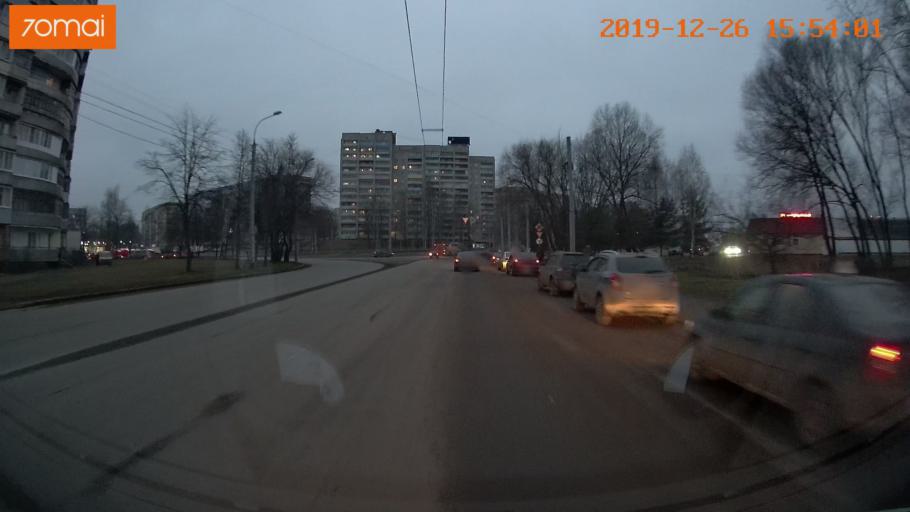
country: RU
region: Jaroslavl
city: Rybinsk
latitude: 58.0469
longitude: 38.8217
